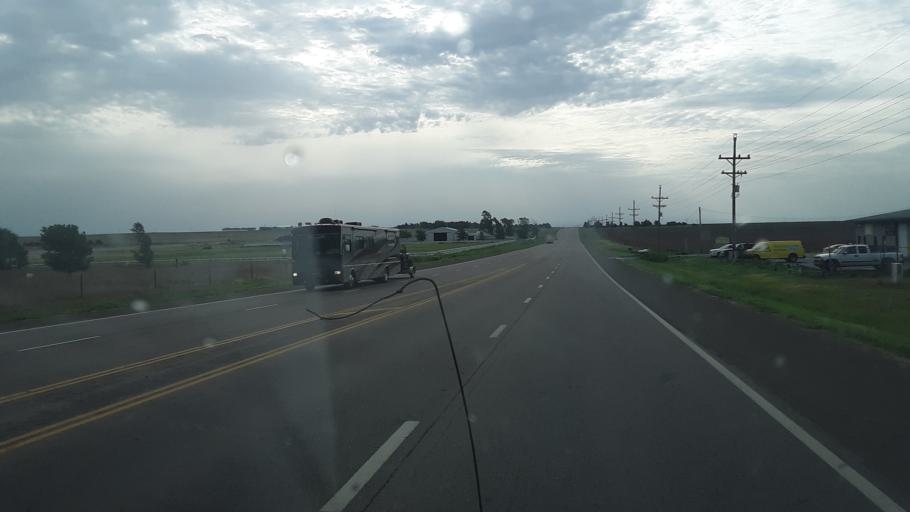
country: US
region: Kansas
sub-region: Finney County
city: Garden City
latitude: 37.9602
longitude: -100.8076
